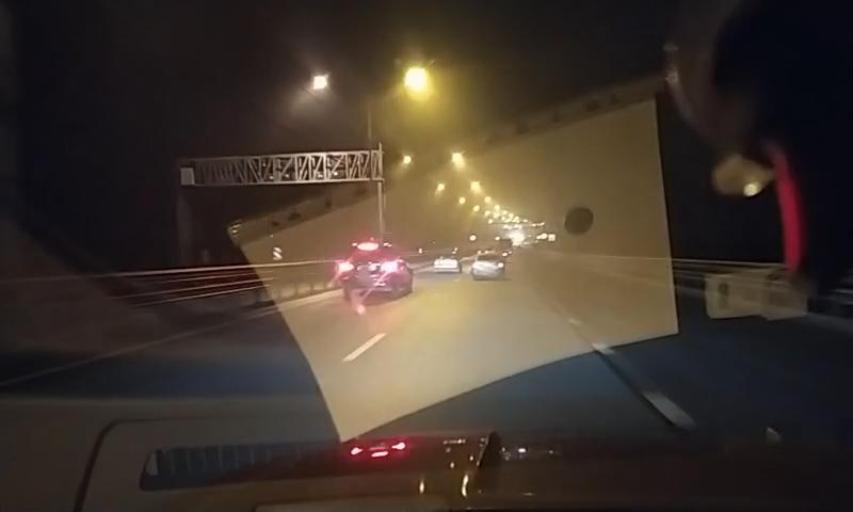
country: RU
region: Leningrad
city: Bugry
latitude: 60.1245
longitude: 30.3847
